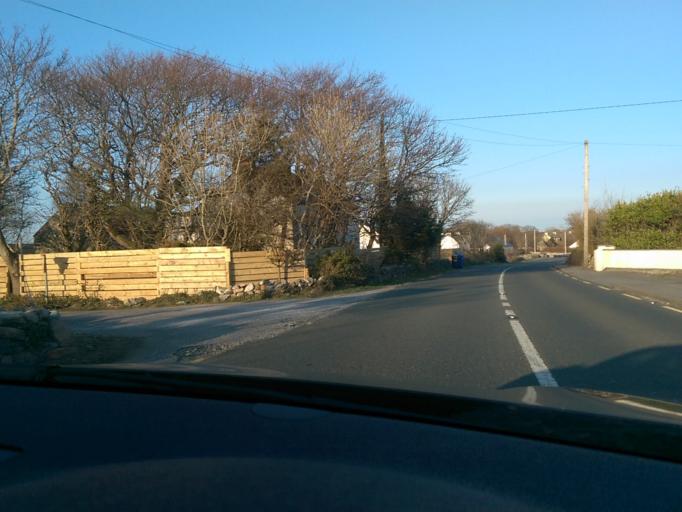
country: IE
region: Connaught
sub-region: County Galway
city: Oughterard
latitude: 53.2428
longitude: -9.4105
